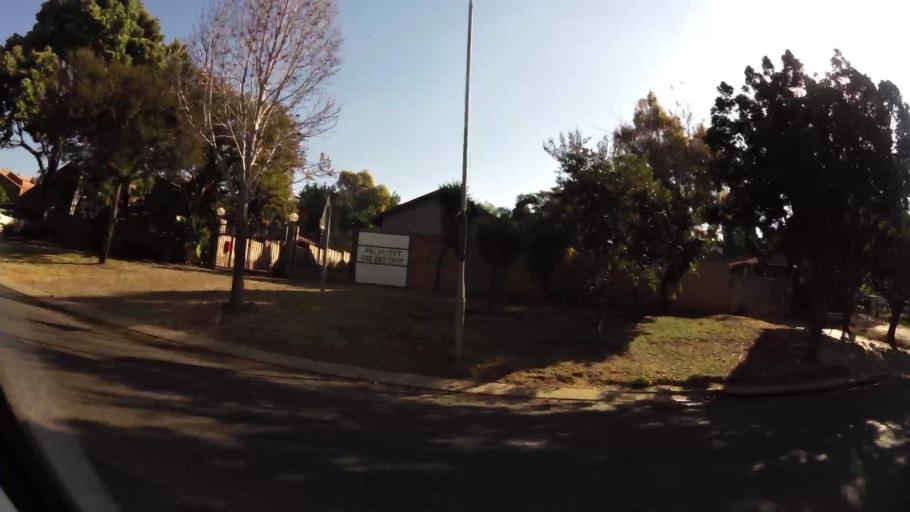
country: ZA
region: Gauteng
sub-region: City of Tshwane Metropolitan Municipality
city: Centurion
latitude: -25.8211
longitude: 28.2949
